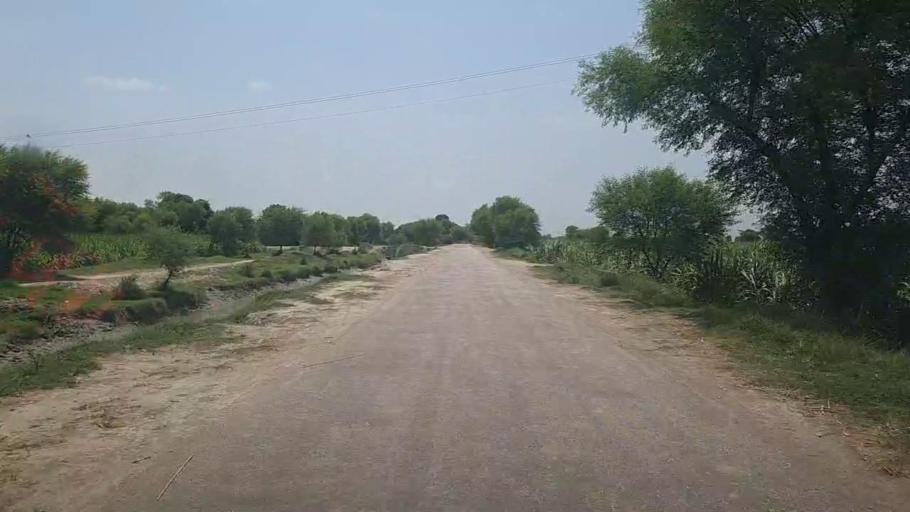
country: PK
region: Sindh
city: Ubauro
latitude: 28.2887
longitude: 69.8087
